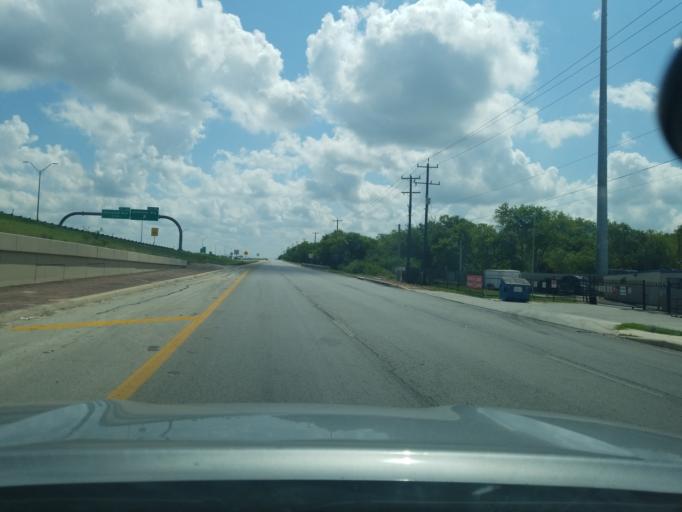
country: US
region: Texas
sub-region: Bexar County
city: Lackland Air Force Base
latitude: 29.3197
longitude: -98.5315
